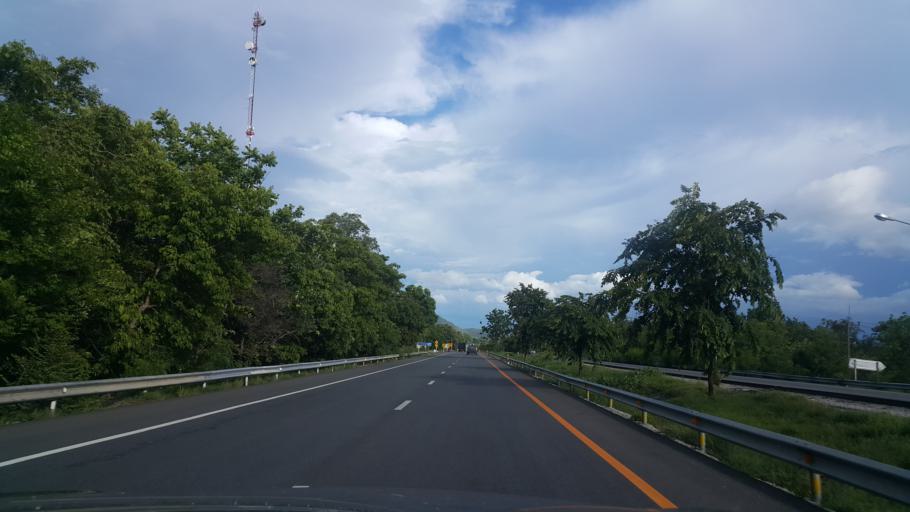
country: TH
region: Tak
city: Ban Tak
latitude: 17.0427
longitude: 99.0823
